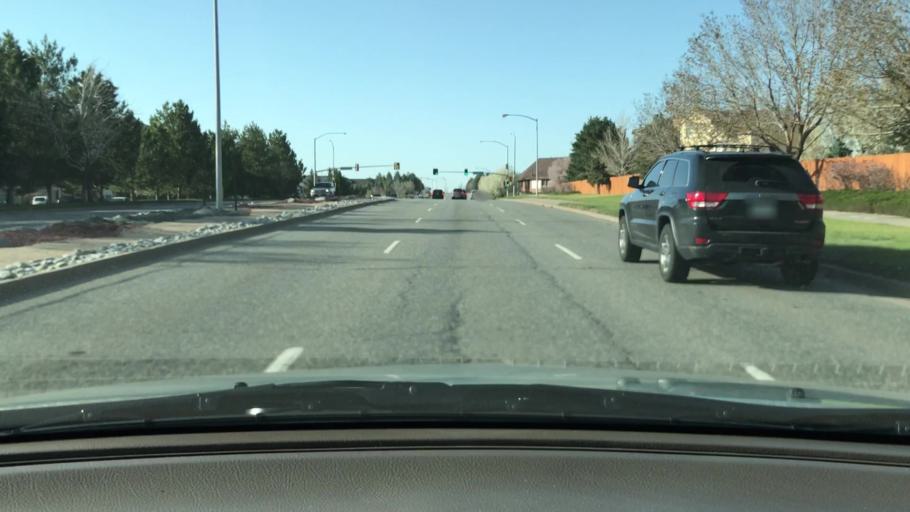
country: US
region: Colorado
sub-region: Adams County
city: Aurora
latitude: 39.6556
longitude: -104.7724
